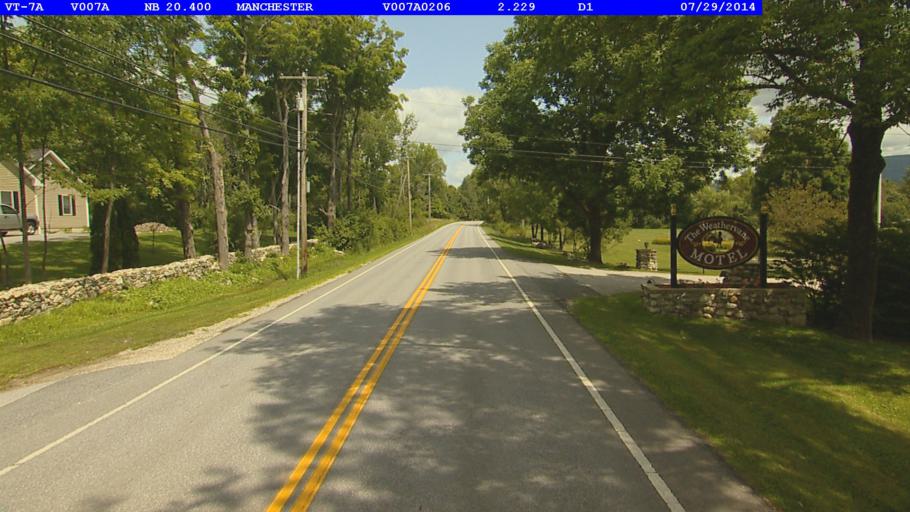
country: US
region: Vermont
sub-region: Bennington County
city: Manchester Center
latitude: 43.1483
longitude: -73.0872
